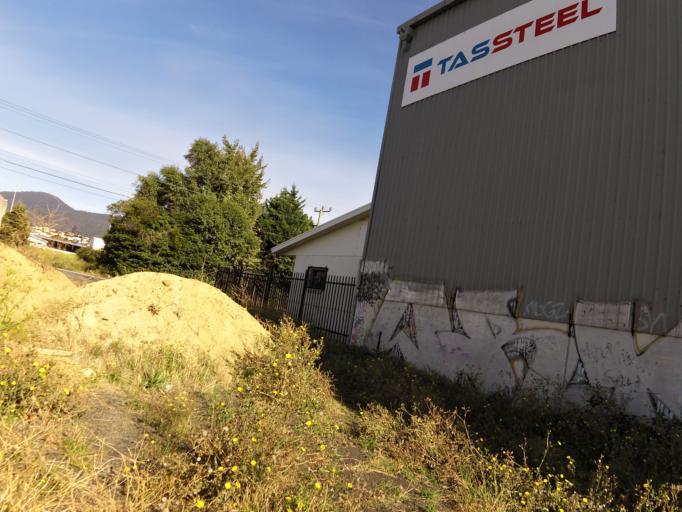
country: AU
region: Tasmania
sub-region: Glenorchy
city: Goodwood
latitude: -42.8378
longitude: 147.2940
